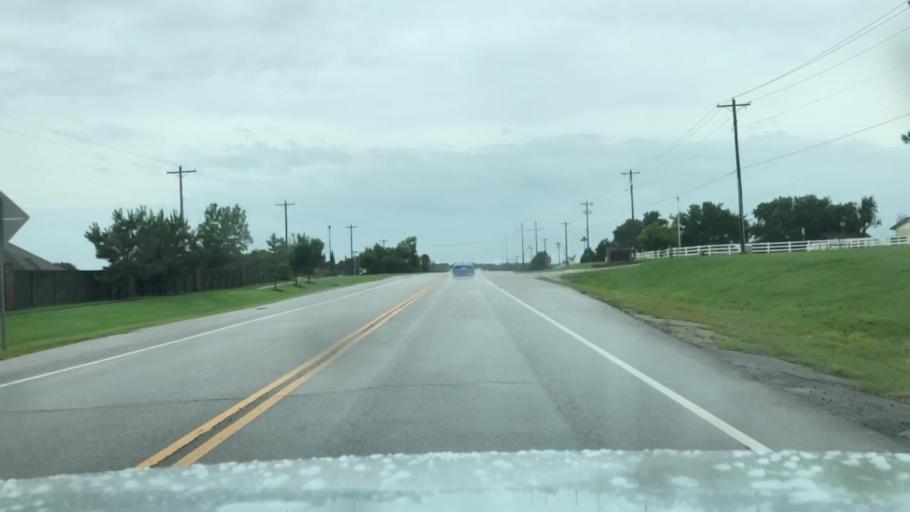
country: US
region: Oklahoma
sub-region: Tulsa County
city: Jenks
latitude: 36.0029
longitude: -96.0030
